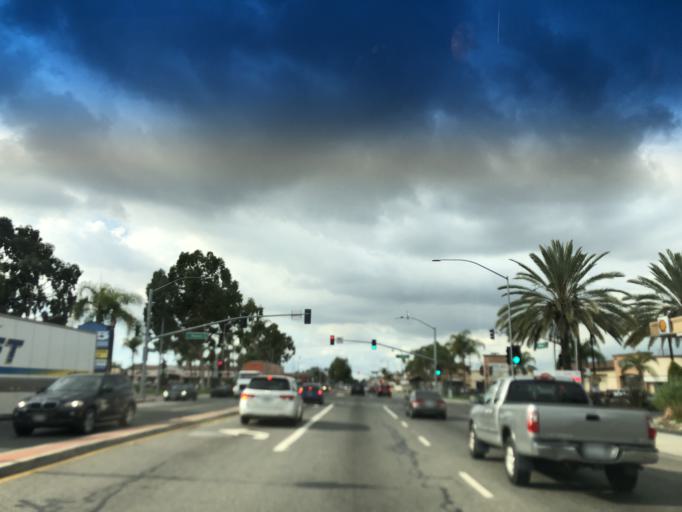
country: US
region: California
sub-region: Los Angeles County
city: West Whittier-Los Nietos
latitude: 33.9985
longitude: -118.0771
